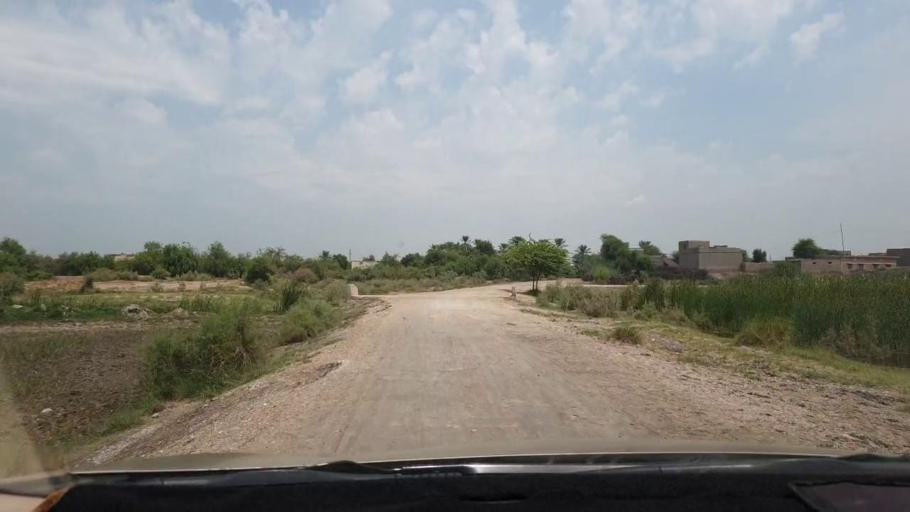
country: PK
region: Sindh
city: Naudero
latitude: 27.7284
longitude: 68.3520
